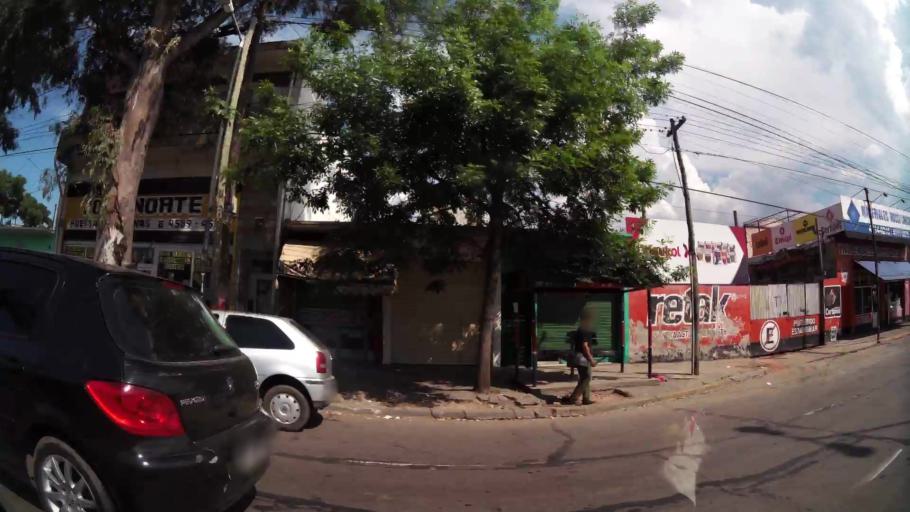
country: AR
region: Buenos Aires
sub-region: Partido de Tigre
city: Tigre
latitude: -34.4655
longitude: -58.5825
